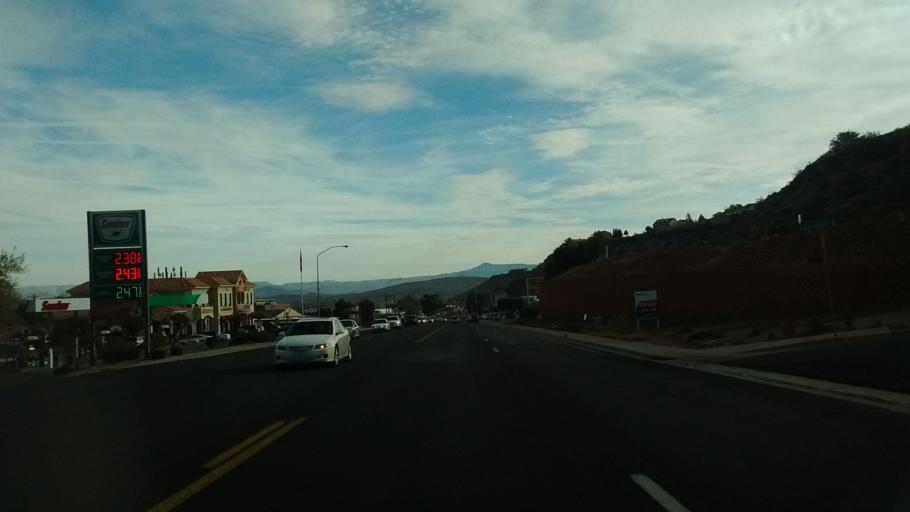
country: US
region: Utah
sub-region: Washington County
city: Saint George
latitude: 37.1152
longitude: -113.5963
